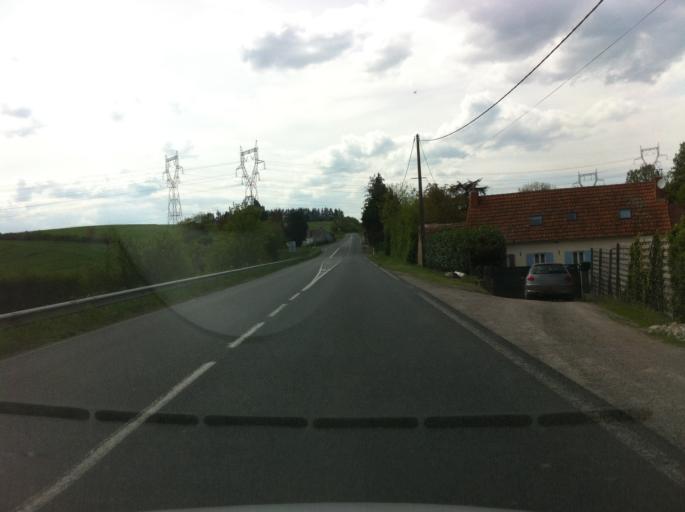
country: FR
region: Auvergne
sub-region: Departement de l'Allier
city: Saint-Pourcain-sur-Sioule
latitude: 46.3150
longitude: 3.2613
